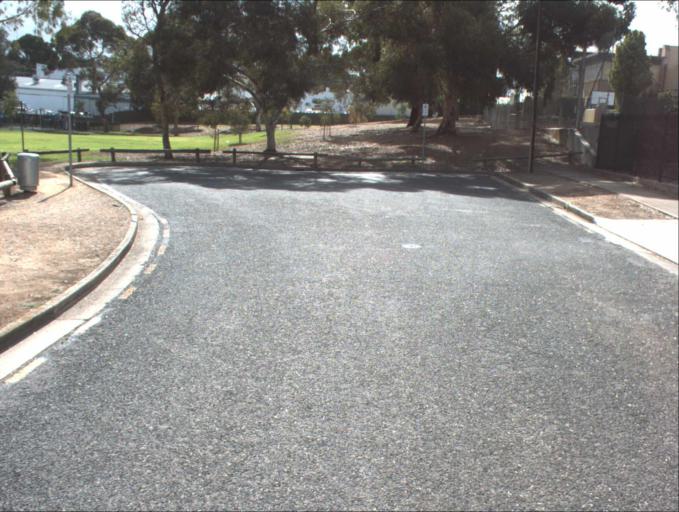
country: AU
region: South Australia
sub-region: Port Adelaide Enfield
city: Blair Athol
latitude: -34.8609
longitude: 138.5983
